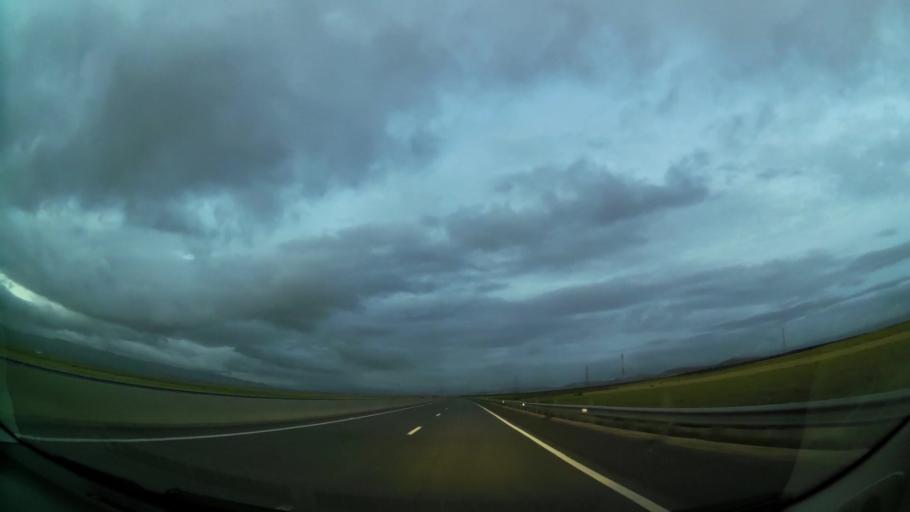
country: MA
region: Oriental
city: El Aioun
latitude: 34.6327
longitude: -2.3331
